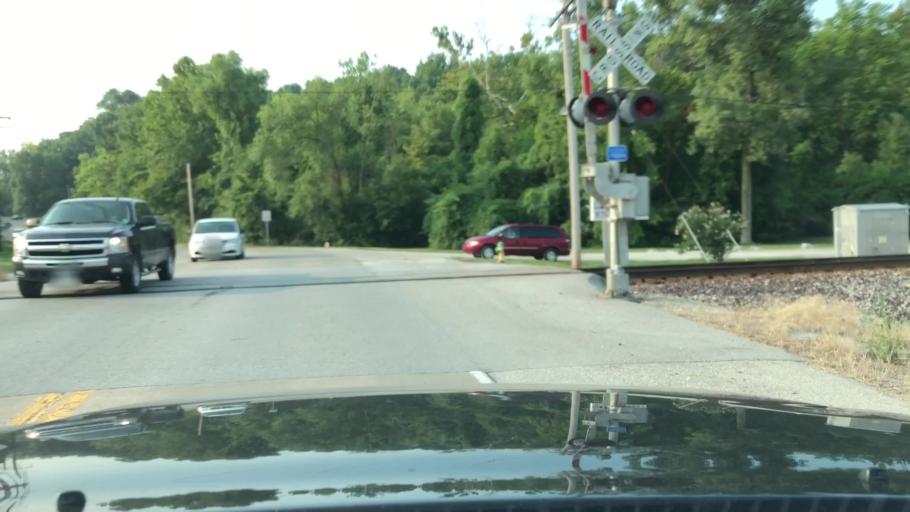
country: US
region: Missouri
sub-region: Saint Charles County
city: Saint Charles
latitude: 38.8118
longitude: -90.5407
